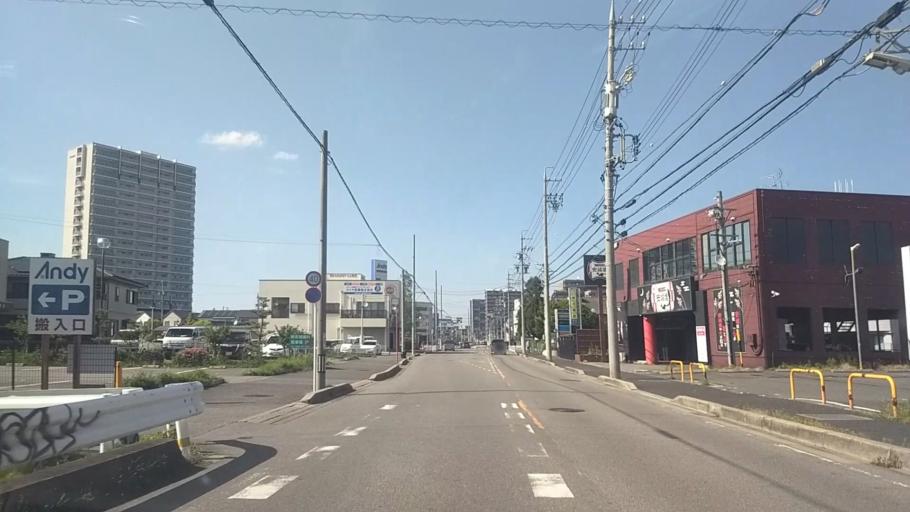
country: JP
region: Aichi
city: Anjo
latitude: 34.9800
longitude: 137.0845
